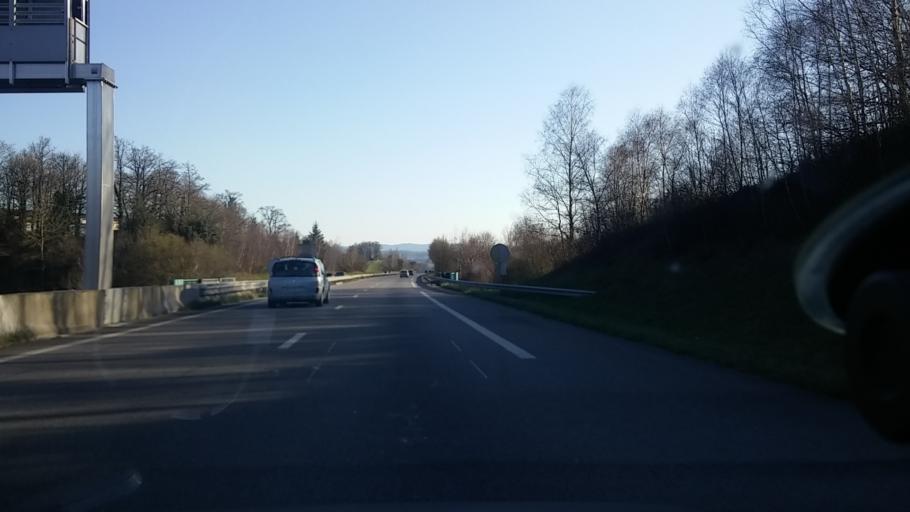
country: FR
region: Limousin
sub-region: Departement de la Creuse
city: Saint-Maurice-la-Souterraine
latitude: 46.1868
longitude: 1.3819
